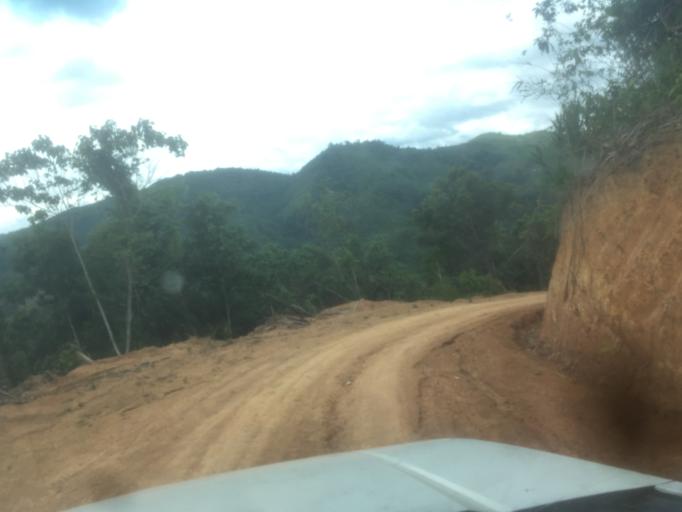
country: LA
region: Phongsali
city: Khoa
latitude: 20.9198
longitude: 102.5598
